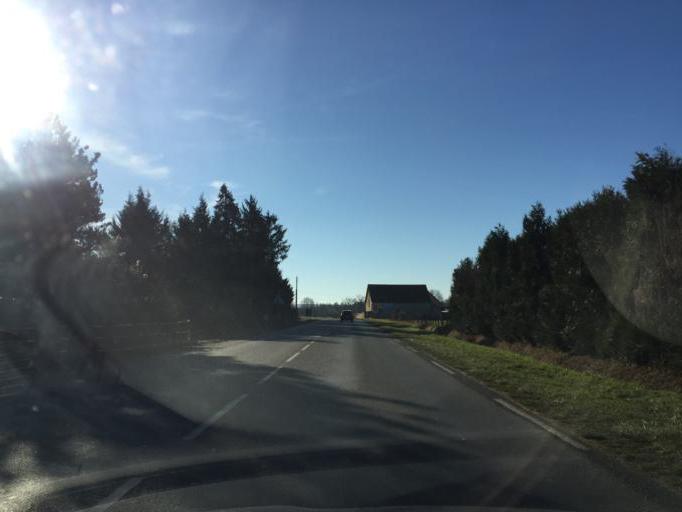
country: FR
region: Auvergne
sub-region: Departement de l'Allier
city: Saint-Remy-en-Rollat
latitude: 46.1694
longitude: 3.3962
